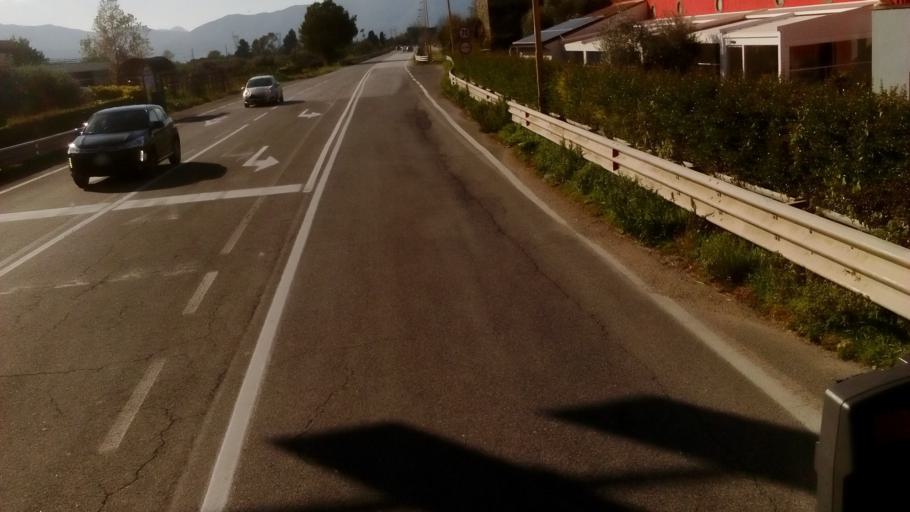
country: IT
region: Molise
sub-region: Provincia di Isernia
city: Taverna Ravindola
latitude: 41.5022
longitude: 14.0997
